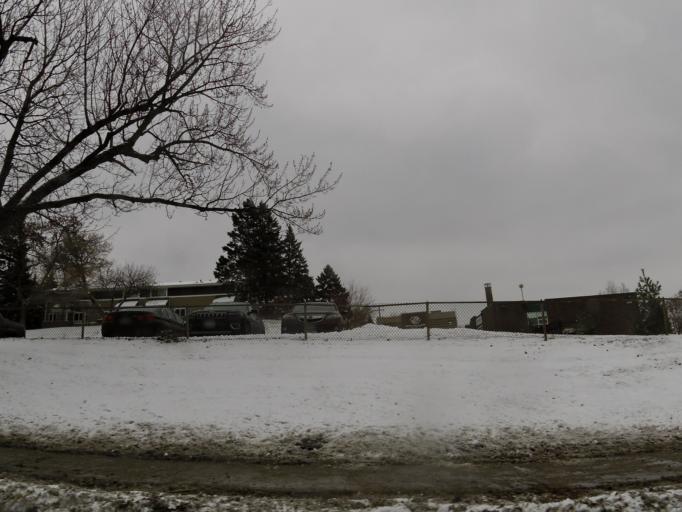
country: US
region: Minnesota
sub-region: Ramsey County
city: Saint Paul
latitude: 44.9589
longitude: -93.0988
